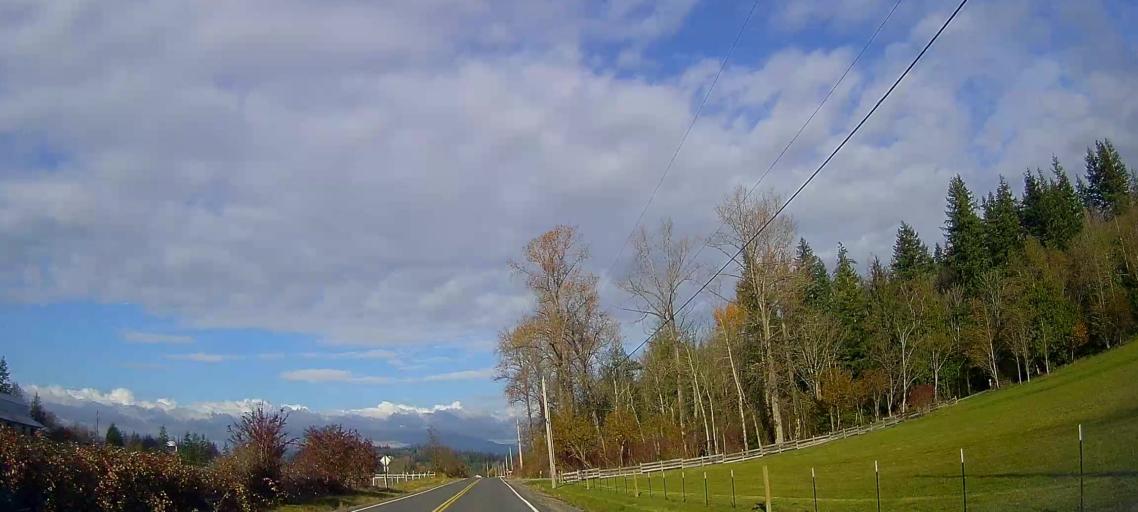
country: US
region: Washington
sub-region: Skagit County
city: Big Lake
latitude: 48.4291
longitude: -122.2422
